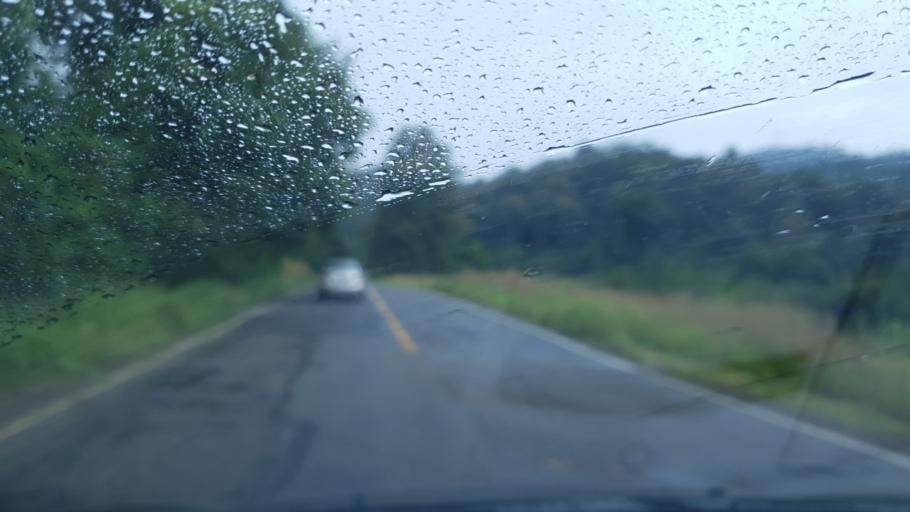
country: TH
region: Mae Hong Son
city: Khun Yuam
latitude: 18.6898
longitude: 97.9210
